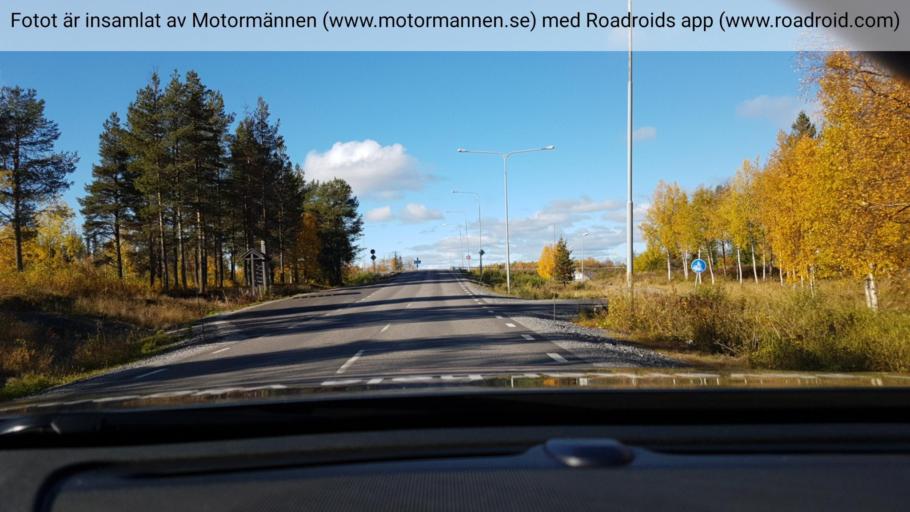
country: SE
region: Norrbotten
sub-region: Gallivare Kommun
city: Gaellivare
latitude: 67.1265
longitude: 20.6727
